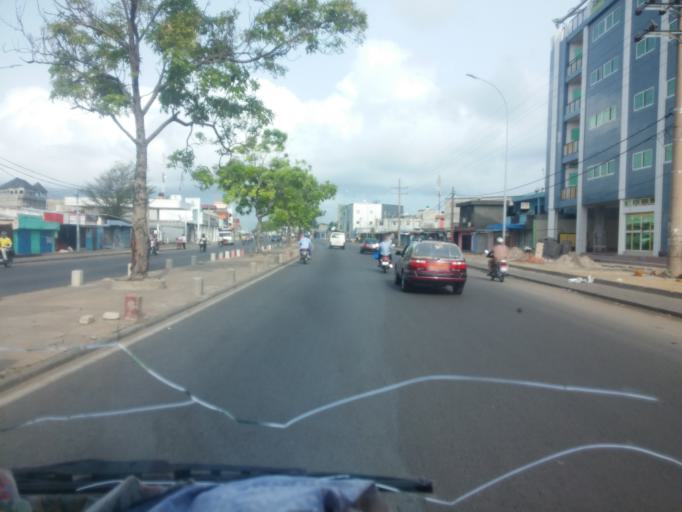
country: BJ
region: Littoral
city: Cotonou
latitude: 6.3762
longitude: 2.4029
